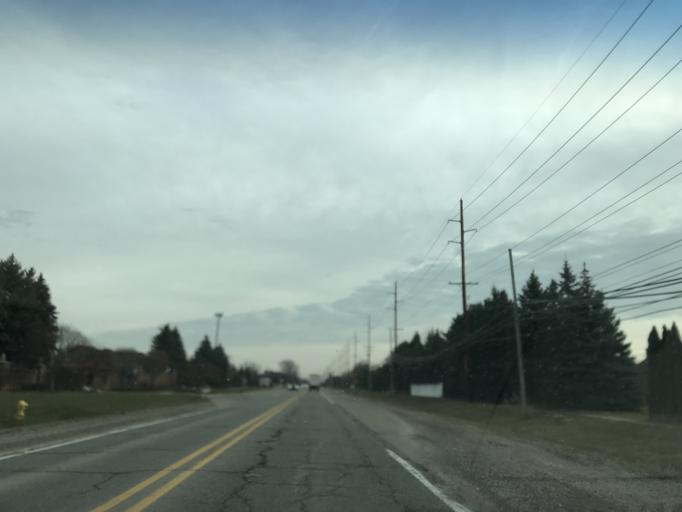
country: US
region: Michigan
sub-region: Macomb County
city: Clinton
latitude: 42.6722
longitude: -82.9309
